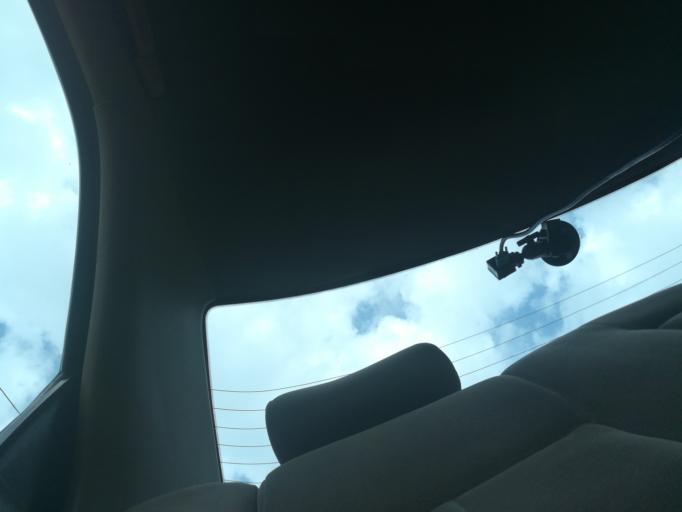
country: NG
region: Lagos
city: Ikorodu
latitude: 6.6619
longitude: 3.5935
